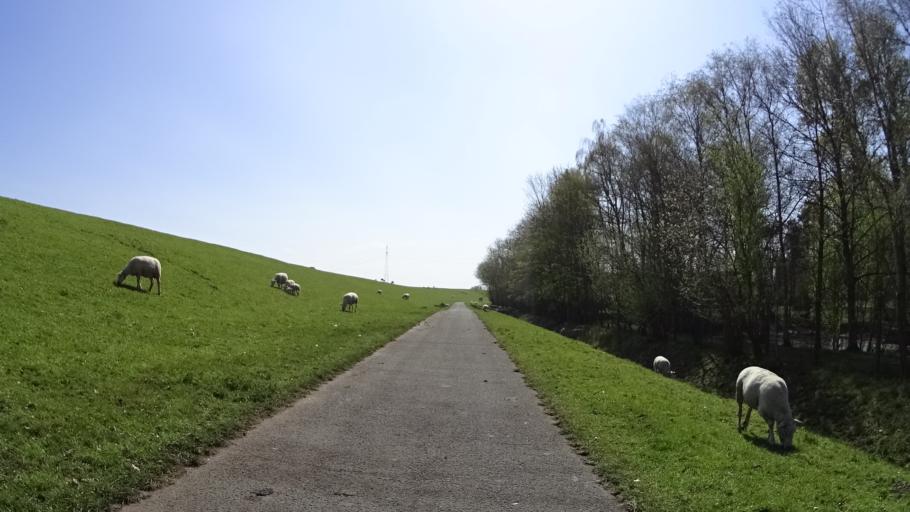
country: DE
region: Lower Saxony
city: Weener
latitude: 53.1586
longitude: 7.3717
